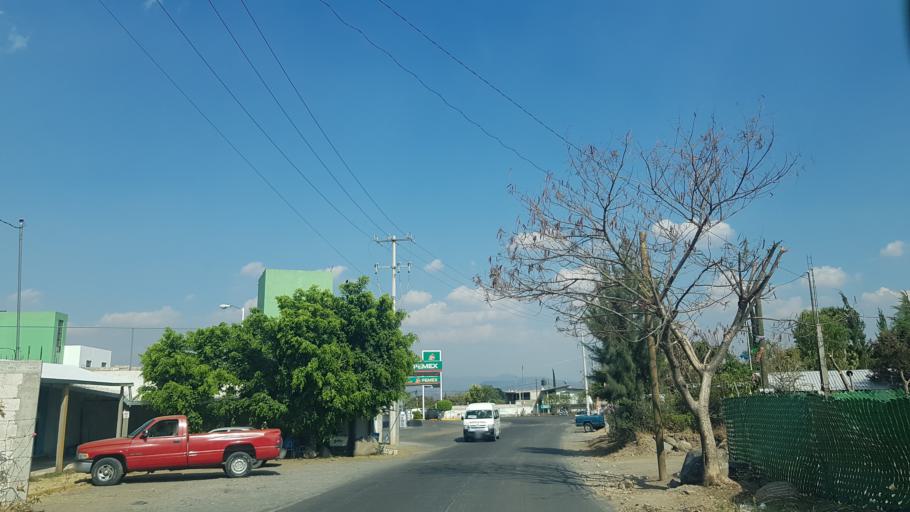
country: MX
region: Puebla
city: Atlixco
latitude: 18.9108
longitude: -98.4749
